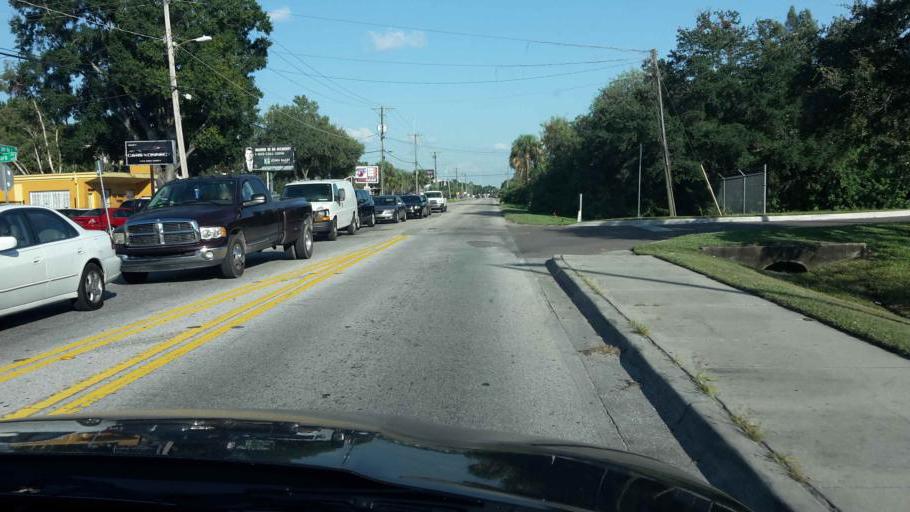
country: US
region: Florida
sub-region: Hillsborough County
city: Egypt Lake-Leto
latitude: 27.9816
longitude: -82.5136
